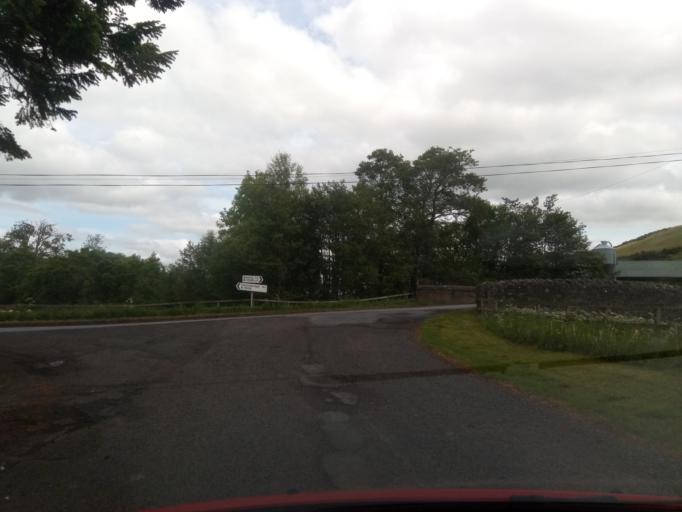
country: GB
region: Scotland
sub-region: The Scottish Borders
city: Selkirk
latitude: 55.5350
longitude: -2.8688
